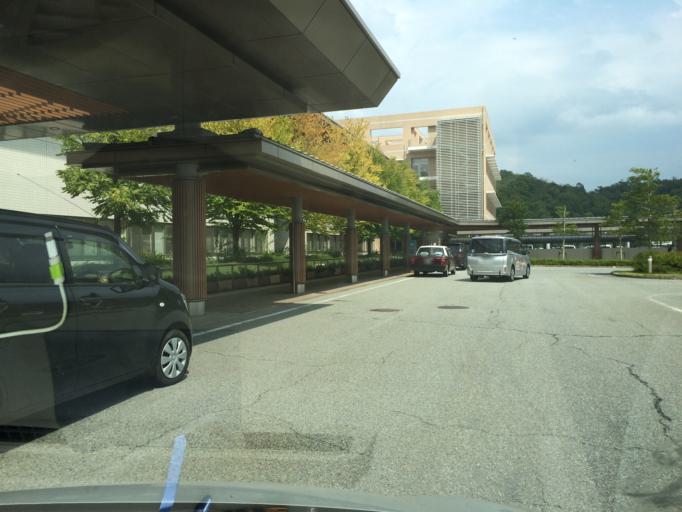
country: JP
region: Hyogo
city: Toyooka
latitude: 35.5261
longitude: 134.8065
